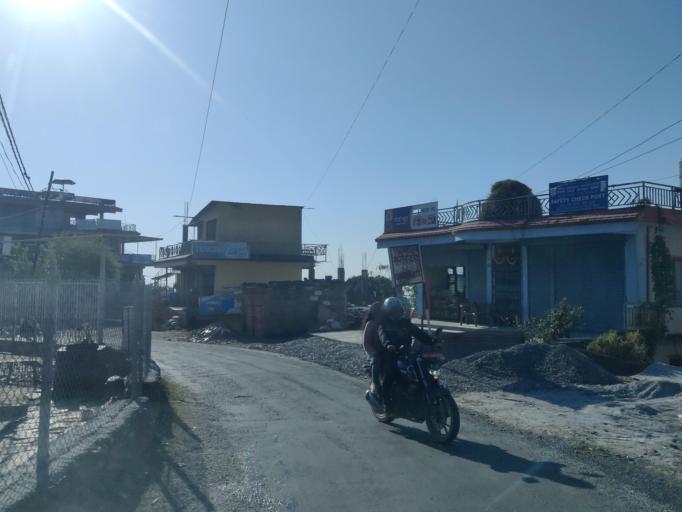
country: NP
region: Western Region
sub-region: Gandaki Zone
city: Pokhara
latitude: 28.2441
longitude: 83.9570
